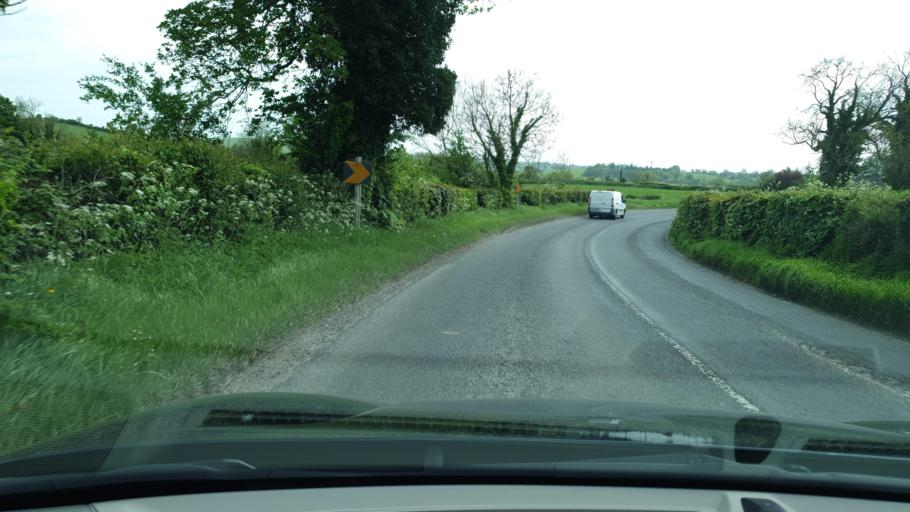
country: IE
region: Ulster
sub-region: An Cabhan
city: Kingscourt
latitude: 53.8309
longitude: -6.7598
